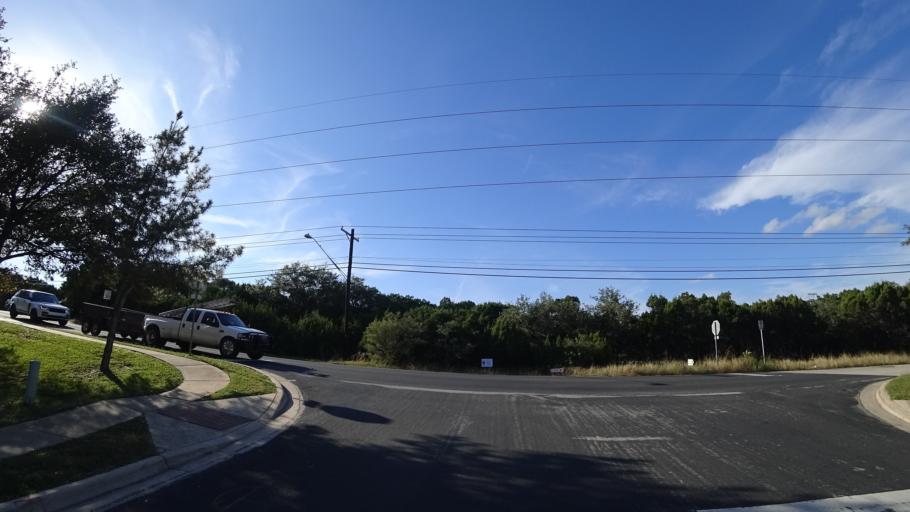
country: US
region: Texas
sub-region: Travis County
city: Barton Creek
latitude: 30.2532
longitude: -97.8461
